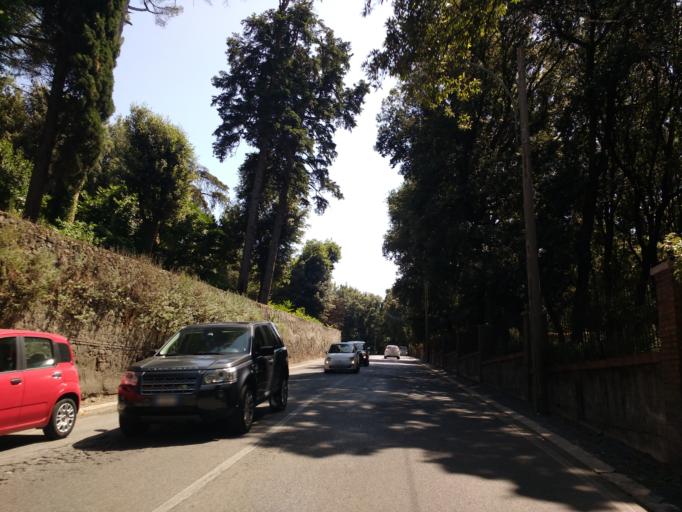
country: IT
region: Latium
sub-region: Citta metropolitana di Roma Capitale
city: Armetta
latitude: 41.8032
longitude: 12.6808
